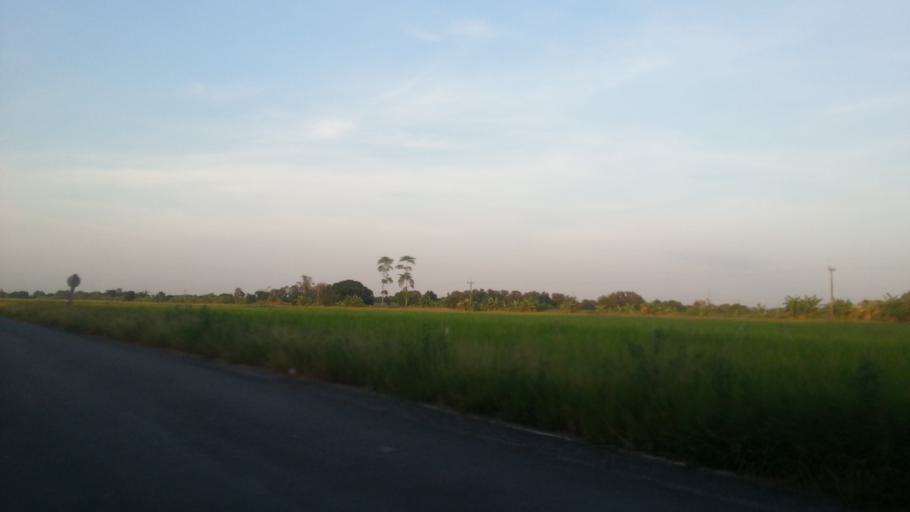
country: TH
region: Pathum Thani
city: Nong Suea
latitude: 14.0522
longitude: 100.8673
